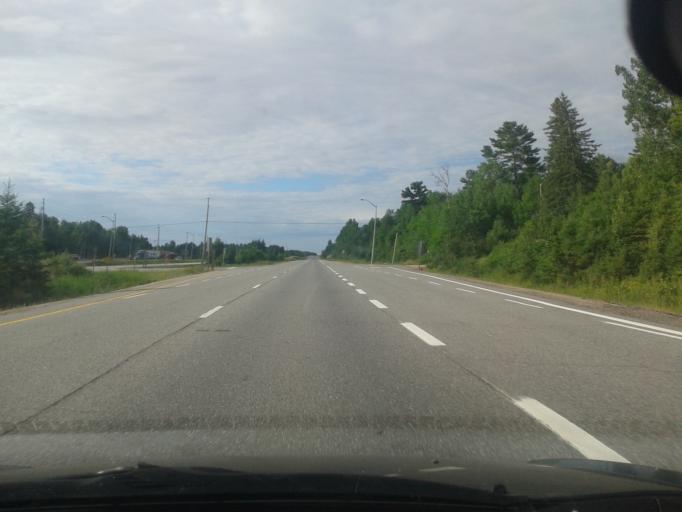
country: CA
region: Ontario
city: Powassan
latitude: 46.1653
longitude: -79.3594
